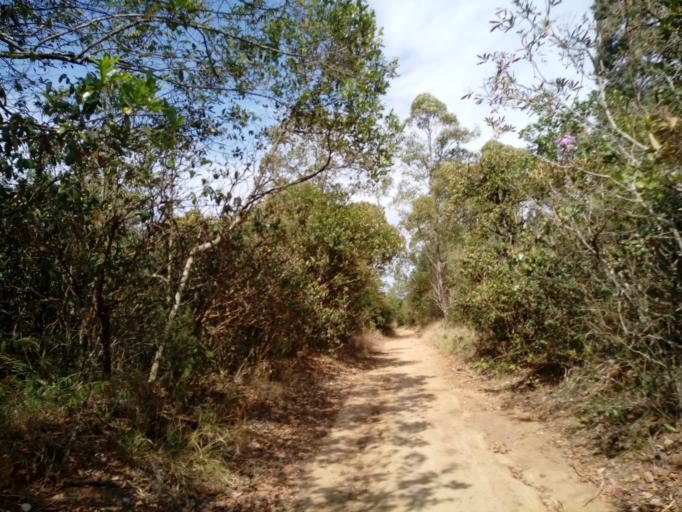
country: BR
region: Sao Paulo
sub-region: Sao Carlos
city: Sao Carlos
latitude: -21.9743
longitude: -47.8830
